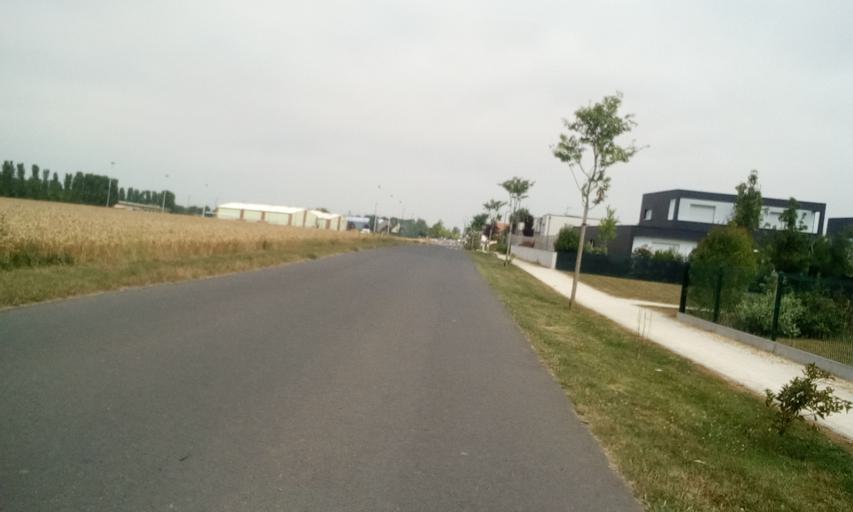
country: FR
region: Lower Normandy
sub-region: Departement du Calvados
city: Douvres-la-Delivrande
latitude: 49.2943
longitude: -0.3919
